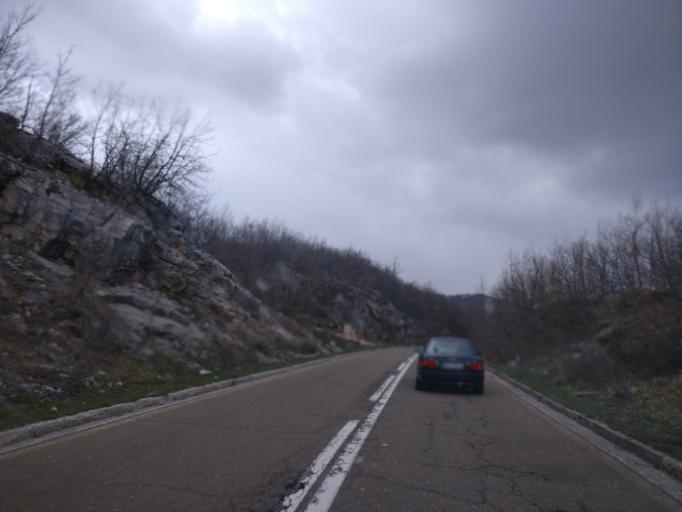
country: ME
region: Opstina Niksic
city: Niksic
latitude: 42.9225
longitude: 18.9460
